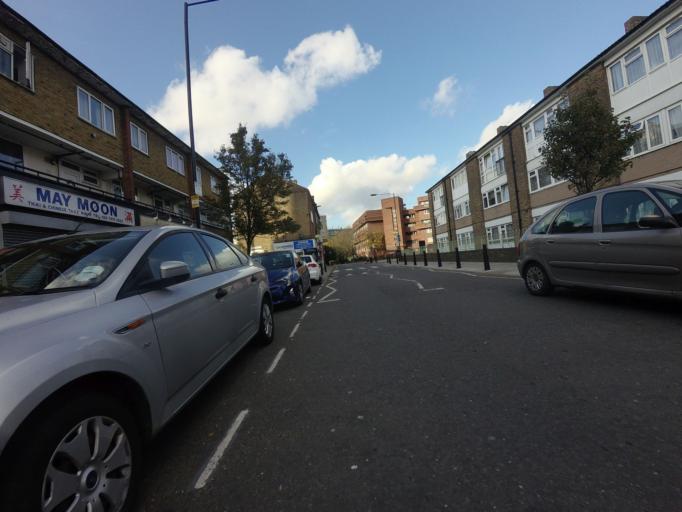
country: GB
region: England
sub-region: Greater London
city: Poplar
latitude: 51.5137
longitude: -0.0334
